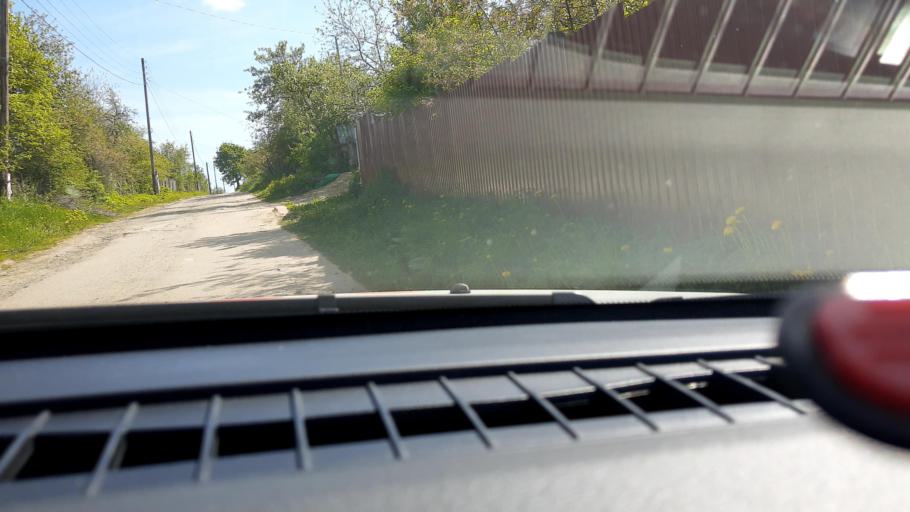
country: RU
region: Nizjnij Novgorod
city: Nizhniy Novgorod
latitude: 56.2295
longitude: 43.9646
